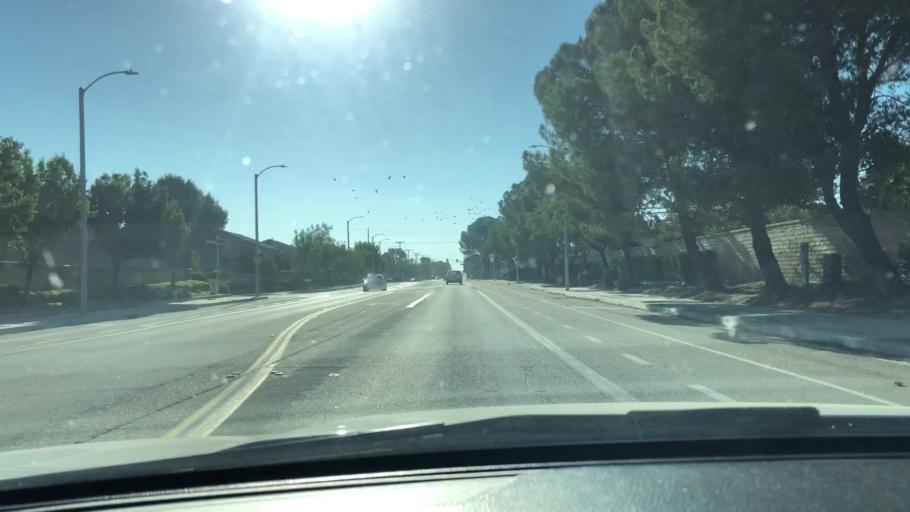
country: US
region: California
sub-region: Los Angeles County
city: Lancaster
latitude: 34.6676
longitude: -118.1687
